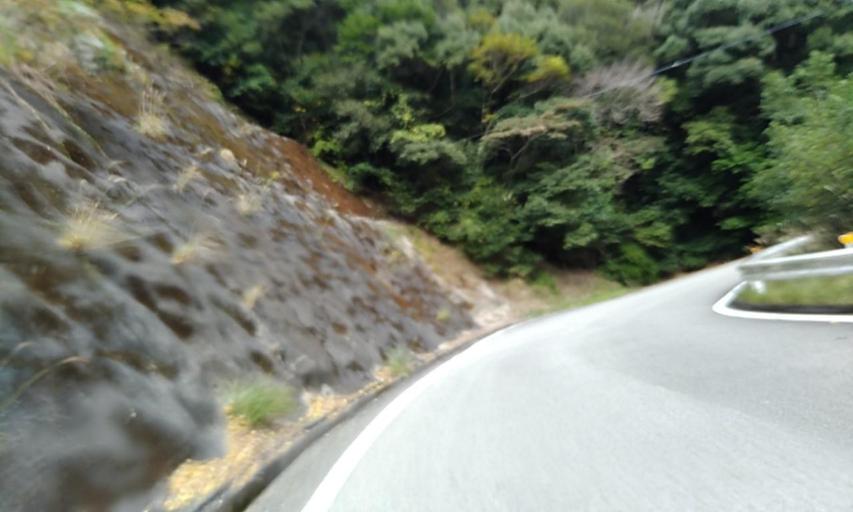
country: JP
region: Wakayama
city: Shingu
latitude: 33.5431
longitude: 135.8324
